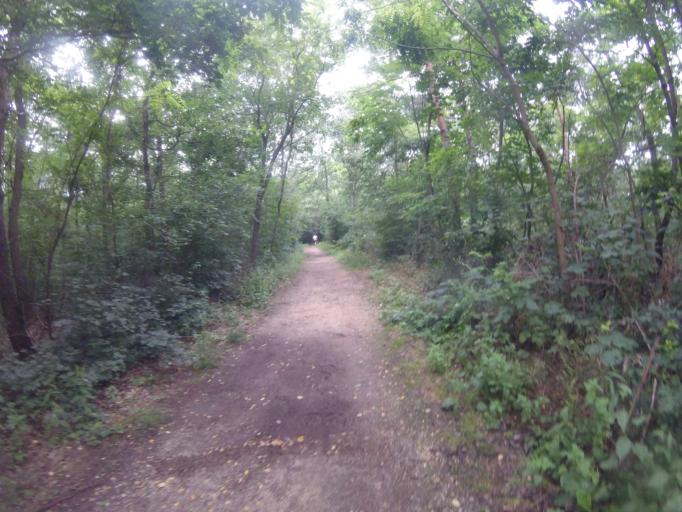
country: HU
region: Pest
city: Toeroekbalint
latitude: 47.4247
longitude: 18.9052
